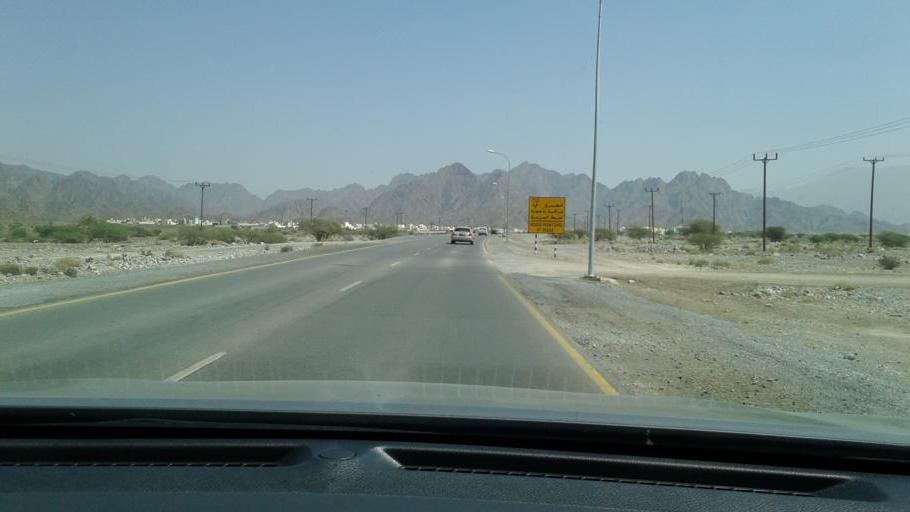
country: OM
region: Al Batinah
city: Rustaq
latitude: 23.3670
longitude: 57.4678
